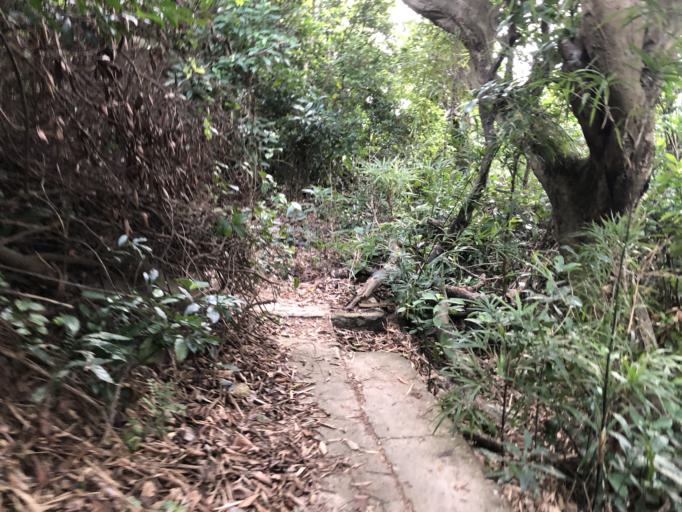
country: HK
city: Hong Kong
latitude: 22.2798
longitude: 114.1197
